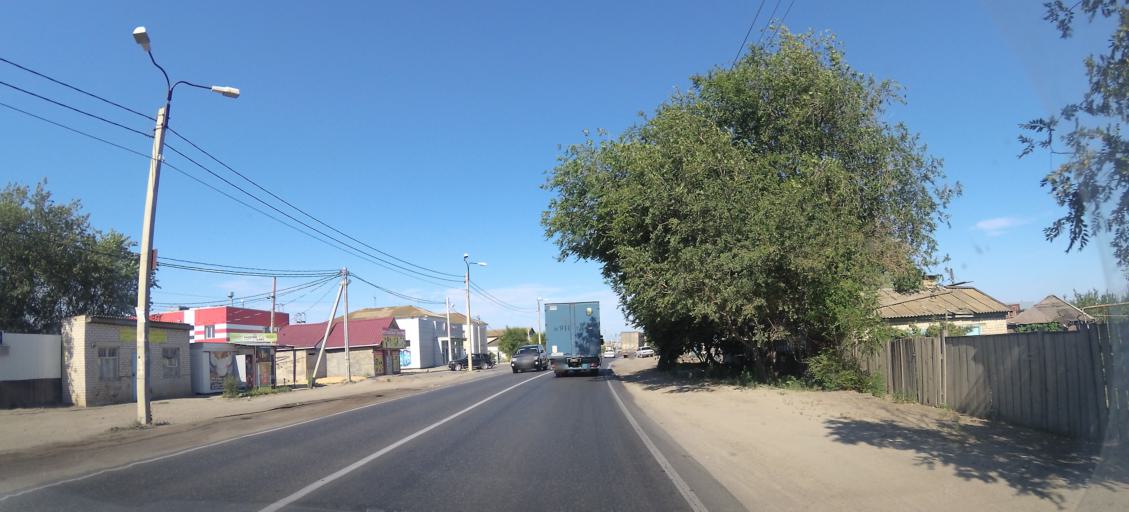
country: RU
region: Volgograd
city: Novyy Rogachik
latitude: 48.6792
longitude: 44.0561
